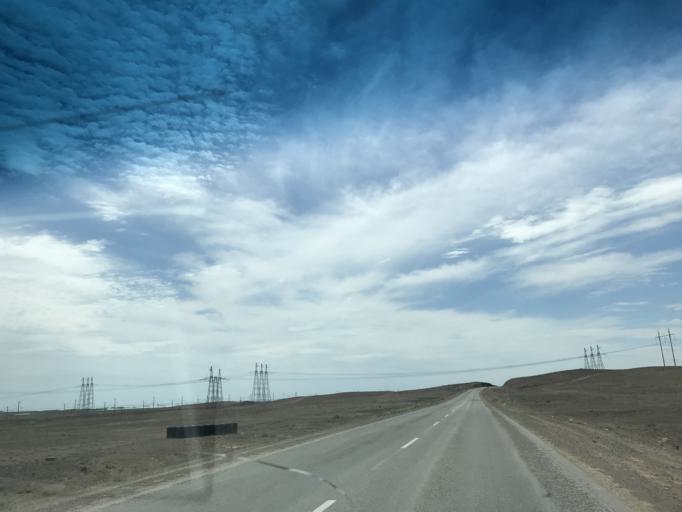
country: KZ
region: Almaty Oblysy
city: Ulken
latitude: 45.1408
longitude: 73.9614
